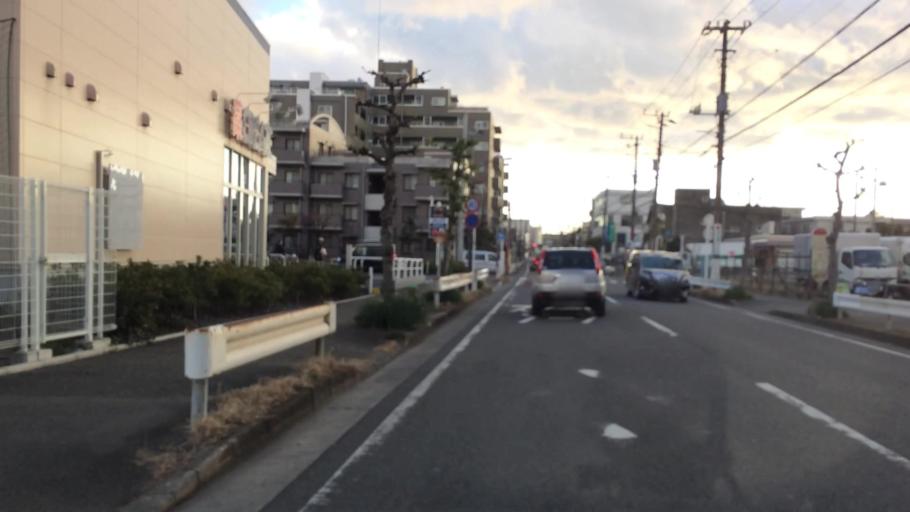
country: JP
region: Kanagawa
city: Fujisawa
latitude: 35.3224
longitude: 139.4651
